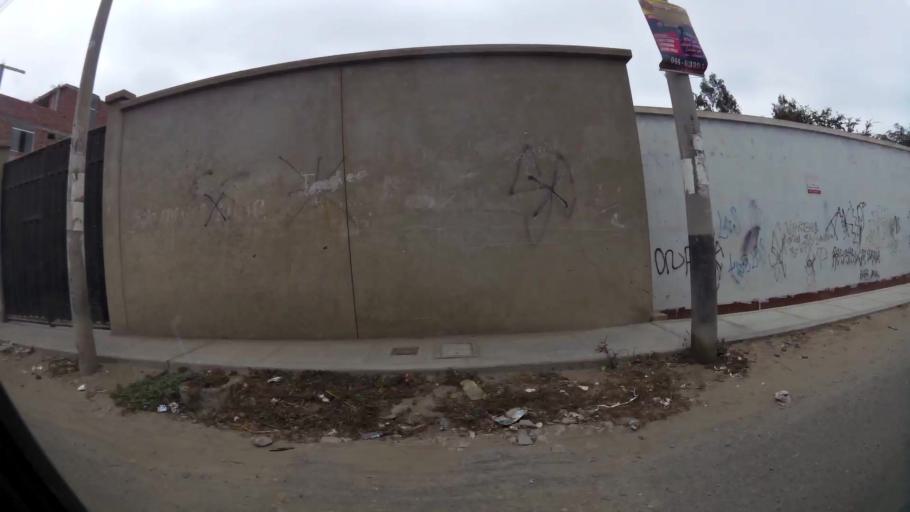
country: PE
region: La Libertad
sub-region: Provincia de Trujillo
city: La Esperanza
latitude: -8.0998
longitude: -79.0568
